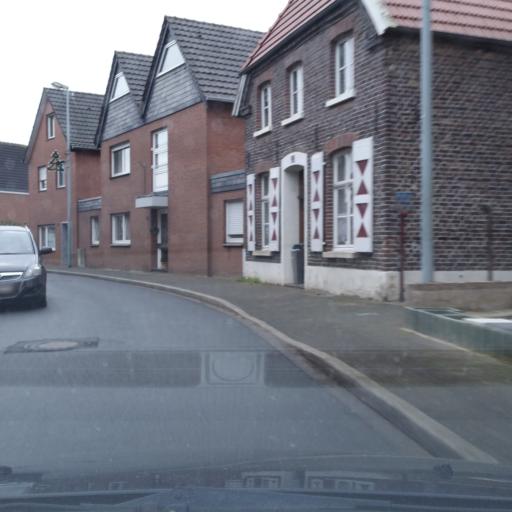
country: DE
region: North Rhine-Westphalia
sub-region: Regierungsbezirk Munster
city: Isselburg
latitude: 51.8198
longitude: 6.5094
